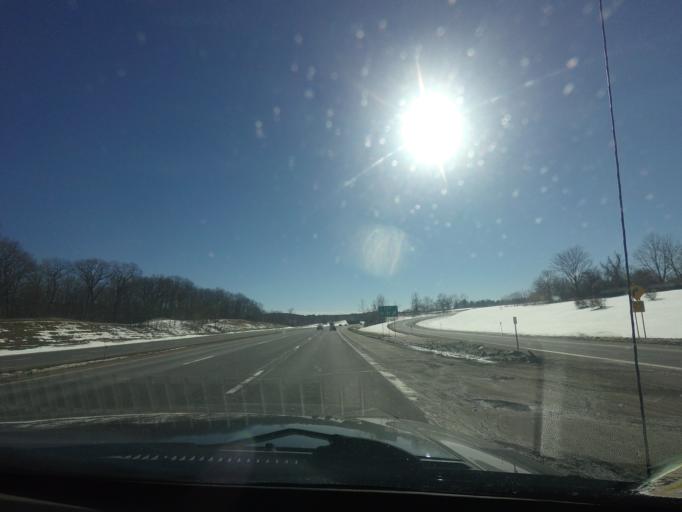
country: US
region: New York
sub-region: Rensselaer County
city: East Greenbush
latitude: 42.5626
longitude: -73.6789
